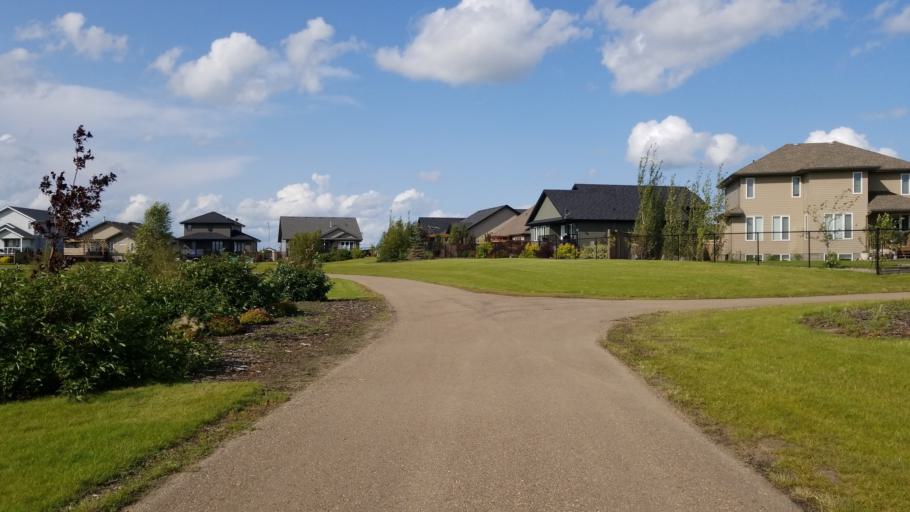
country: CA
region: Saskatchewan
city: Lloydminster
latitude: 53.2633
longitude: -110.0462
